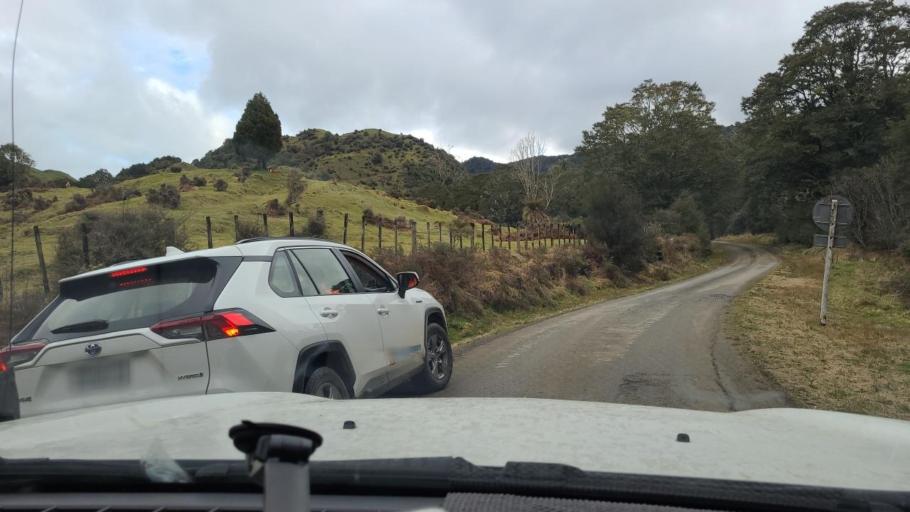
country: NZ
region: Bay of Plenty
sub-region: Opotiki District
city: Opotiki
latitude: -38.4076
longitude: 177.4311
